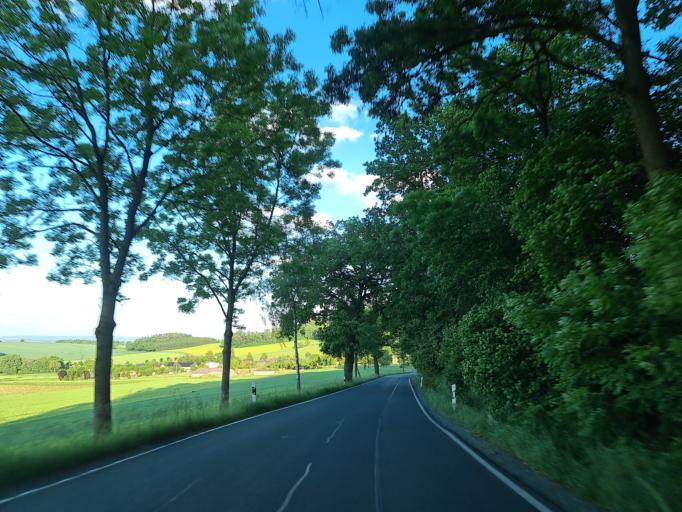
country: DE
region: Saxony
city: Reuth
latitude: 50.4688
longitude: 11.9935
